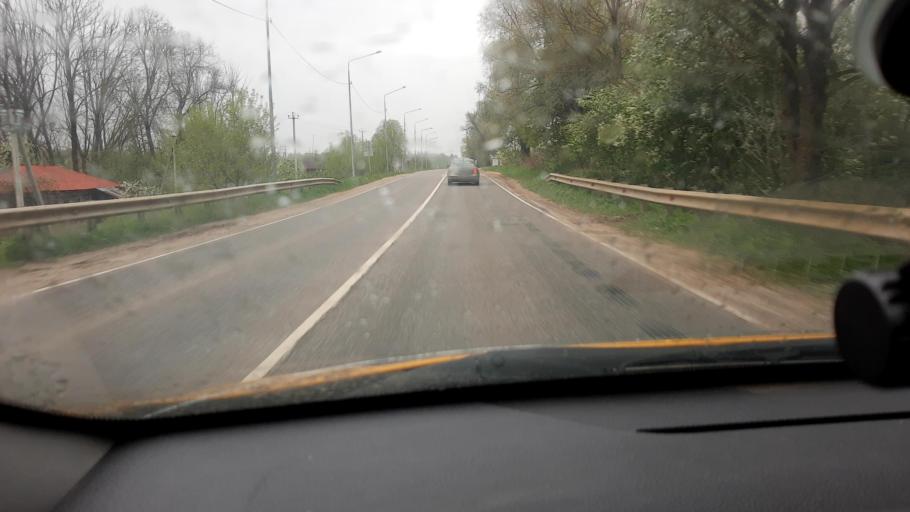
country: RU
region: Tula
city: Zaokskiy
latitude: 54.7627
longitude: 37.4370
